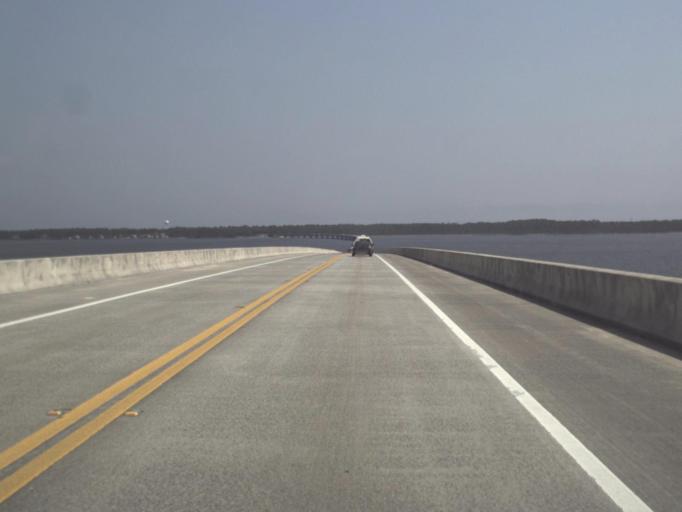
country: US
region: Florida
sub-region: Santa Rosa County
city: Oriole Beach
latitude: 30.4157
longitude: -87.0878
